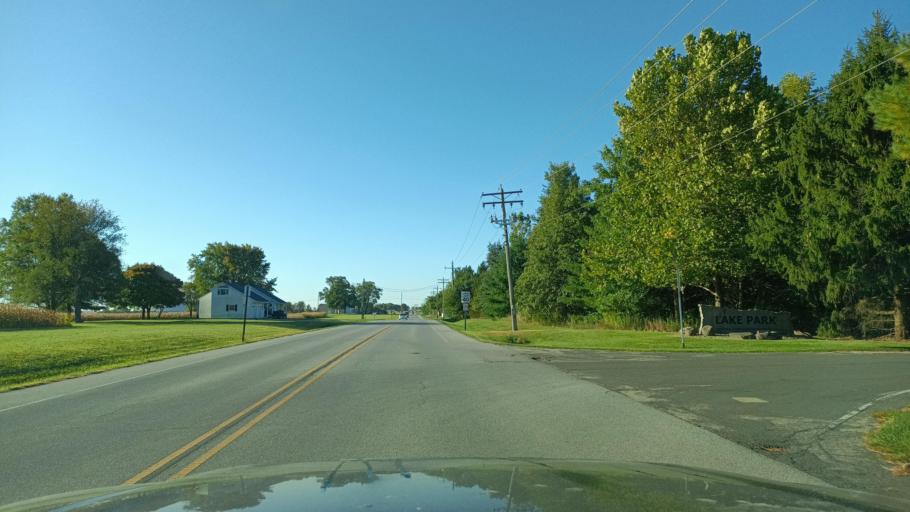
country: US
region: Illinois
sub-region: Champaign County
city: Savoy
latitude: 40.0619
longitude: -88.2384
